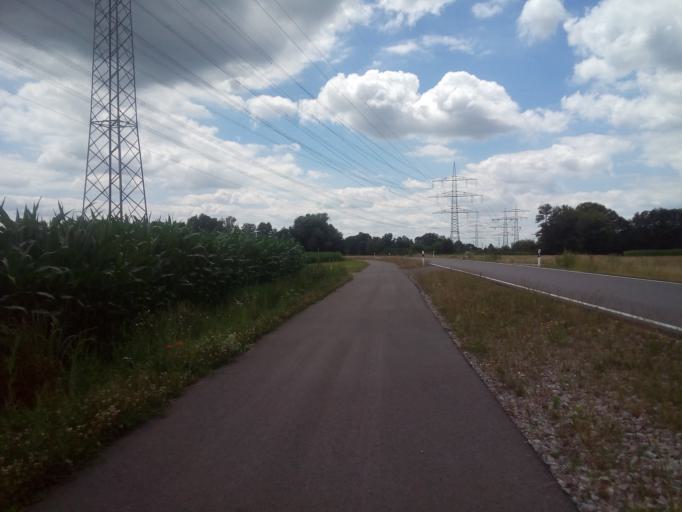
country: DE
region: Baden-Wuerttemberg
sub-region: Freiburg Region
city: Rheinau
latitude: 48.6435
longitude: 7.9385
